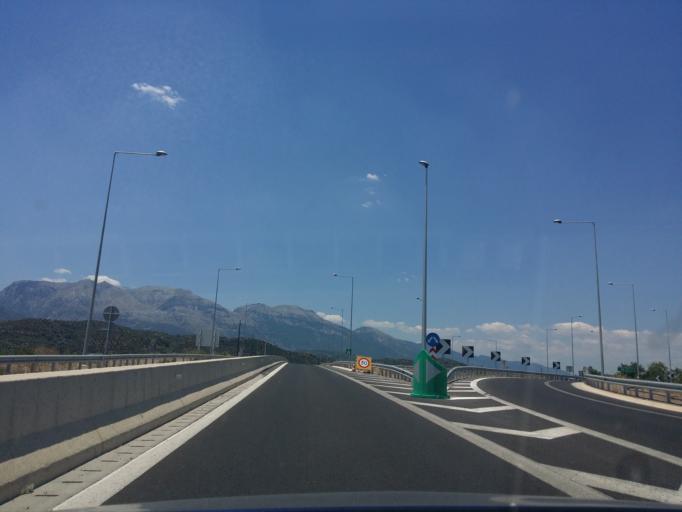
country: GR
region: Peloponnese
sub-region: Nomos Lakonias
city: Sparti
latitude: 37.0932
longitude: 22.4350
